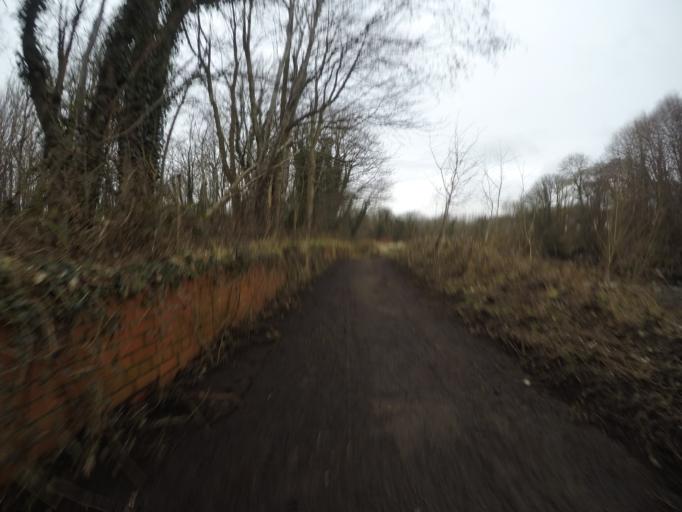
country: GB
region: Scotland
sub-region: North Ayrshire
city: Kilwinning
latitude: 55.6425
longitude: -4.6865
